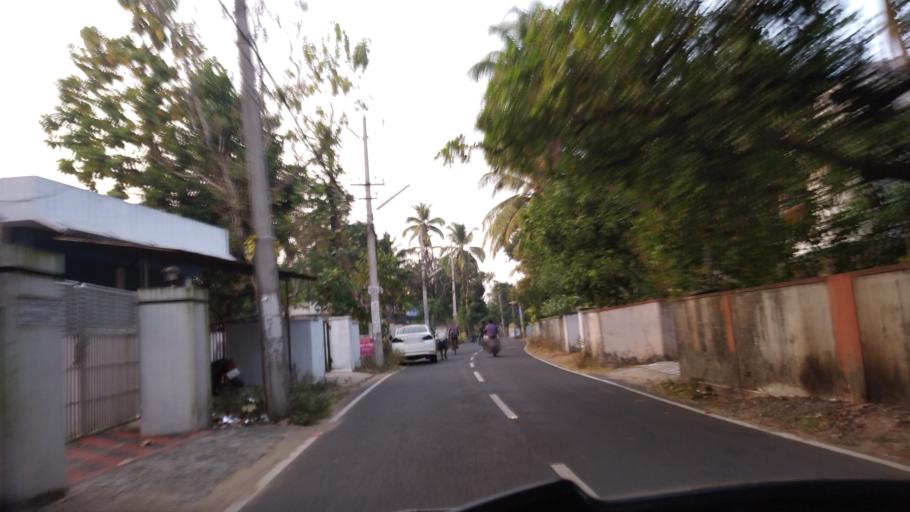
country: IN
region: Kerala
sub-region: Ernakulam
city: Elur
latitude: 10.1283
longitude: 76.2359
